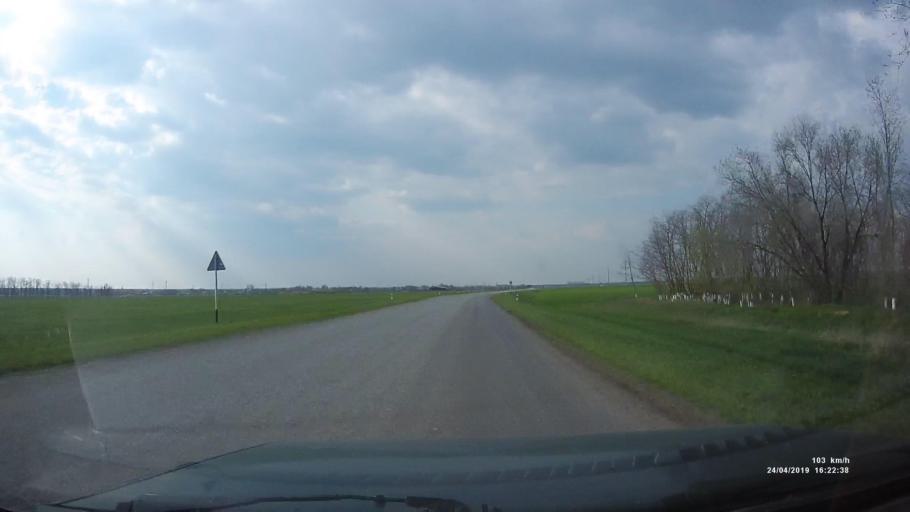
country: RU
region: Rostov
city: Orlovskiy
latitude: 46.8227
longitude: 42.0546
